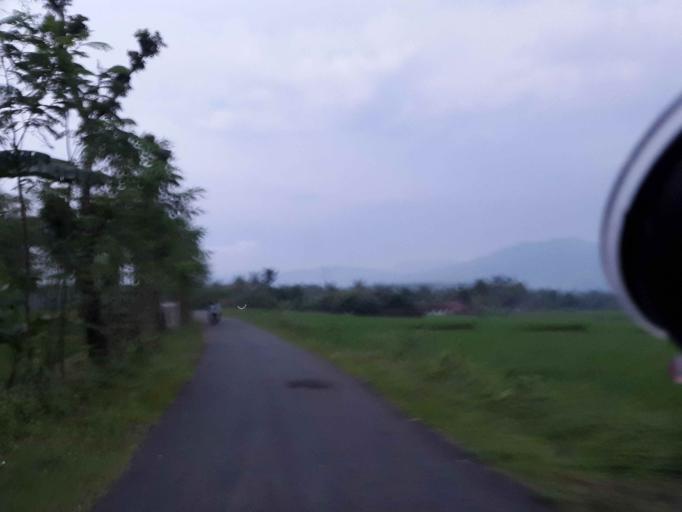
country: ID
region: Central Java
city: Randudongkal
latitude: -7.0767
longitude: 109.3385
